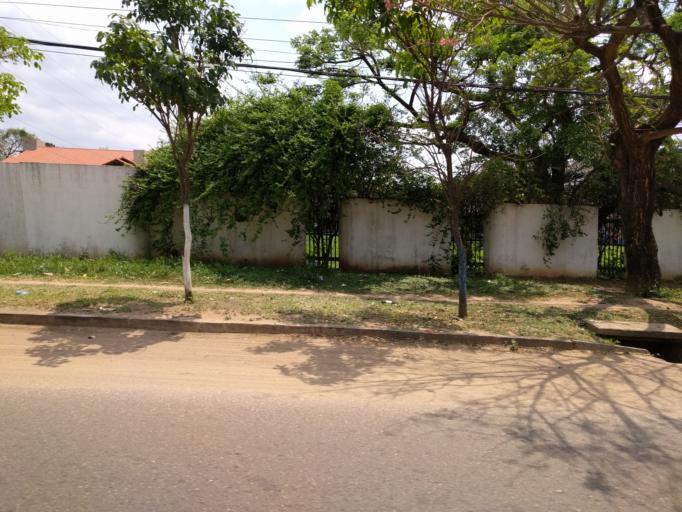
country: BO
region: Santa Cruz
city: Santa Cruz de la Sierra
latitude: -17.8533
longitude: -63.2551
